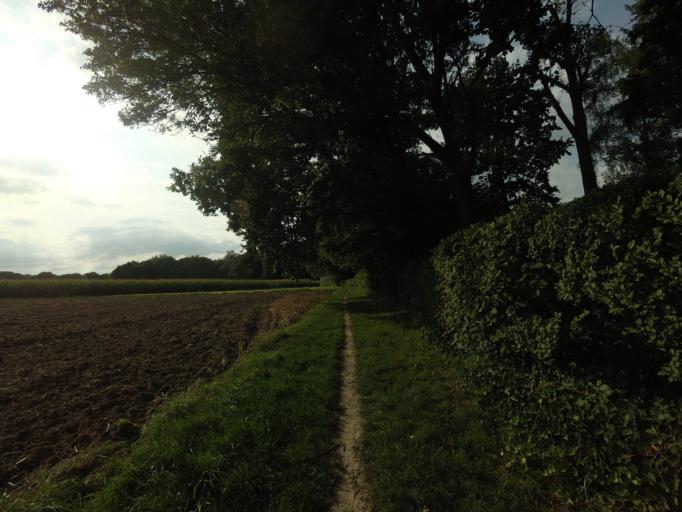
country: BE
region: Flanders
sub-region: Provincie Vlaams-Brabant
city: Kampenhout
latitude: 50.9304
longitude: 4.5620
